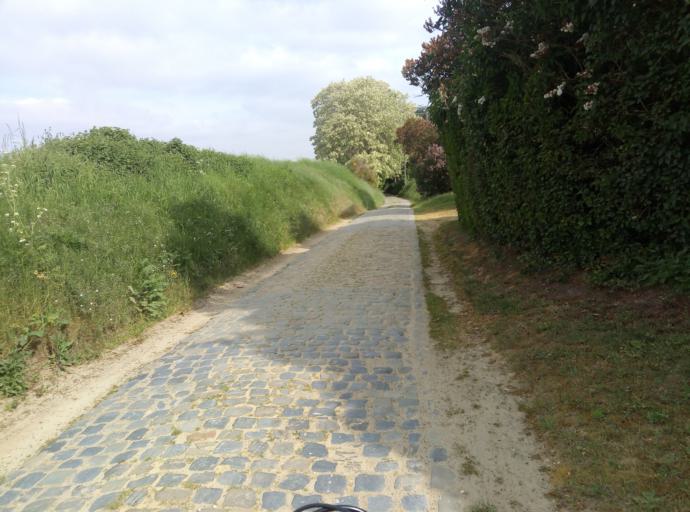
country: BE
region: Flanders
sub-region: Provincie Vlaams-Brabant
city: Bierbeek
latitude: 50.8537
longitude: 4.7365
